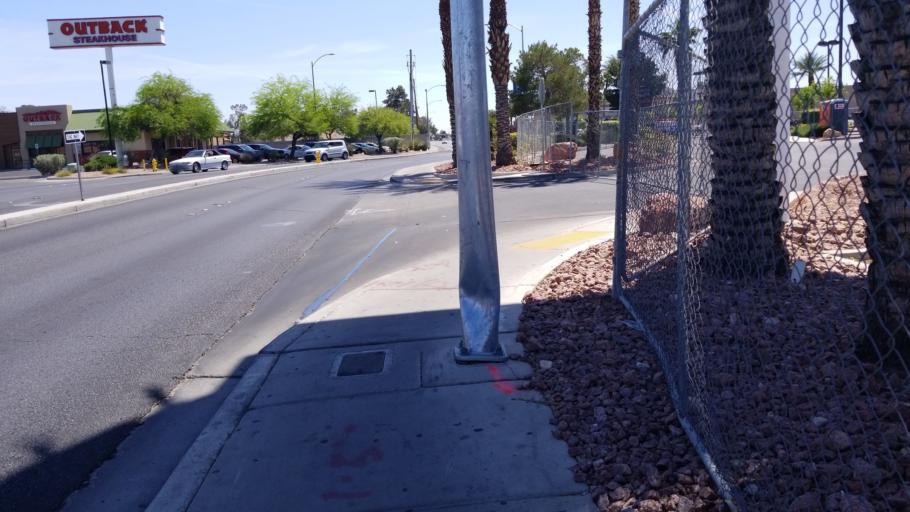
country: US
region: Nevada
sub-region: Clark County
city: Spring Valley
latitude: 36.1954
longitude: -115.2421
